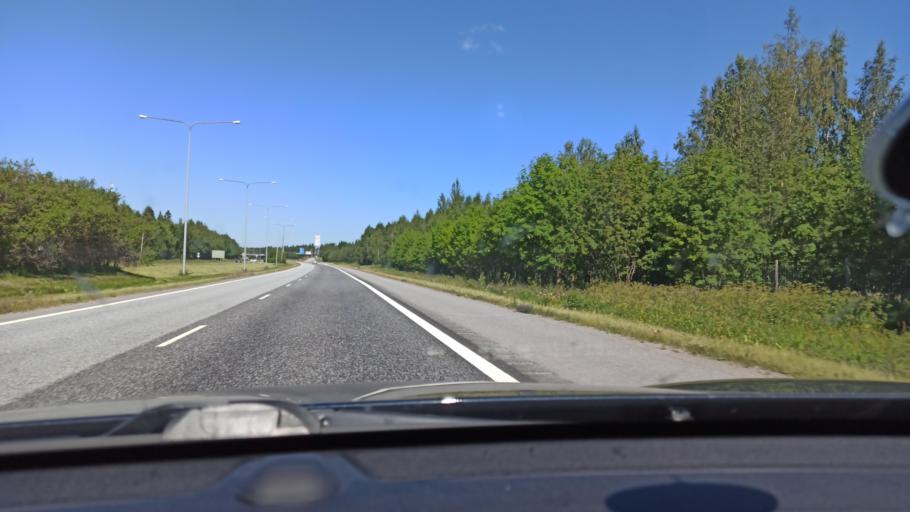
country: FI
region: Ostrobothnia
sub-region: Vaasa
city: Ristinummi
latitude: 63.0639
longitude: 21.7065
